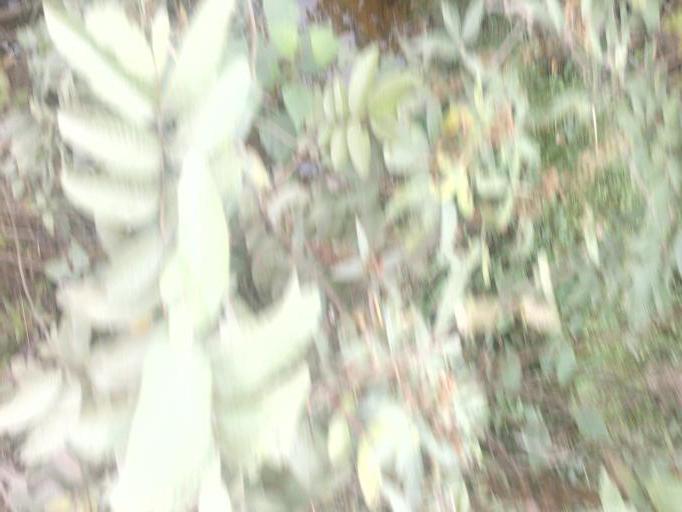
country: LA
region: Xiangkhoang
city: Muang Phonsavan
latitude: 19.3395
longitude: 103.6268
